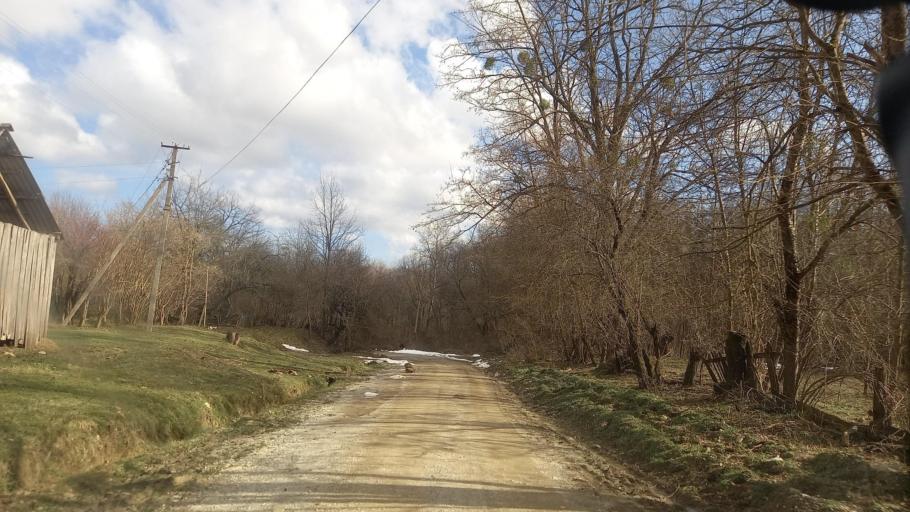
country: RU
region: Krasnodarskiy
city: Smolenskaya
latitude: 44.6016
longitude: 38.8694
